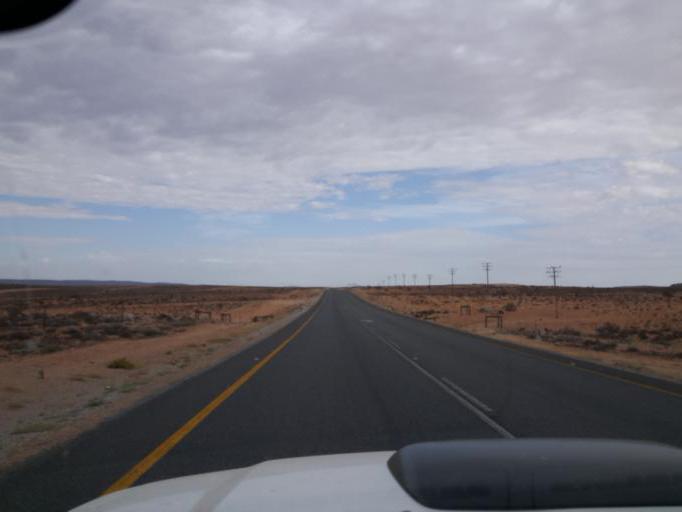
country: ZA
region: Northern Cape
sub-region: Namakwa District Municipality
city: Springbok
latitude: -29.3615
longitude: 17.7890
